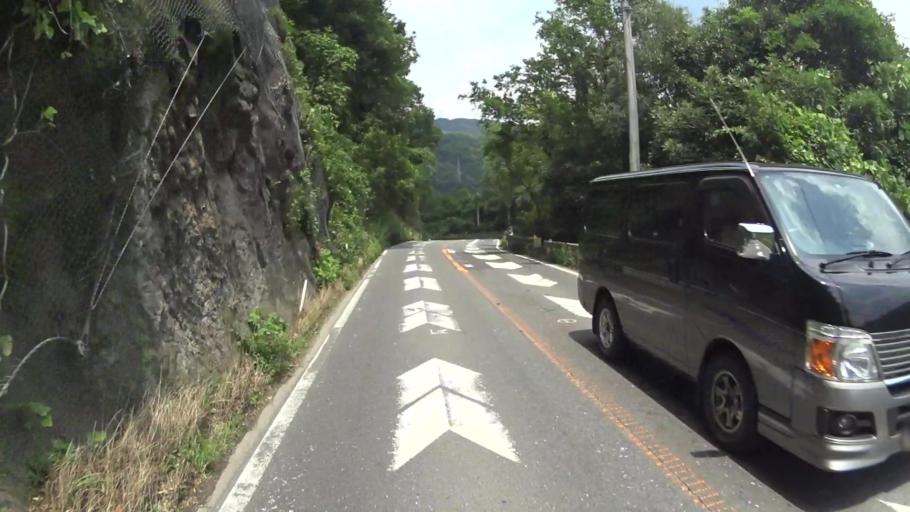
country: JP
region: Nara
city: Nara-shi
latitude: 34.7644
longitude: 135.8994
